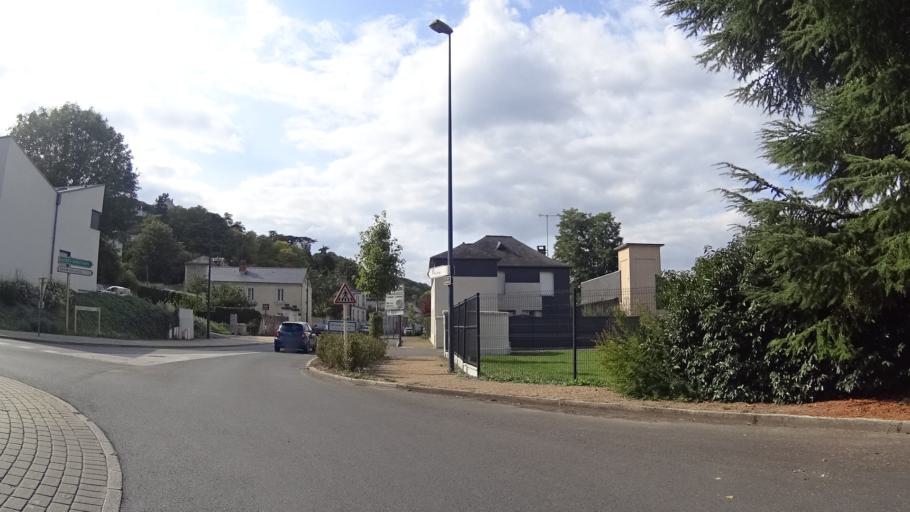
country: FR
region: Pays de la Loire
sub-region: Departement de Maine-et-Loire
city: Villebernier
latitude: 47.2501
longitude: -0.0525
